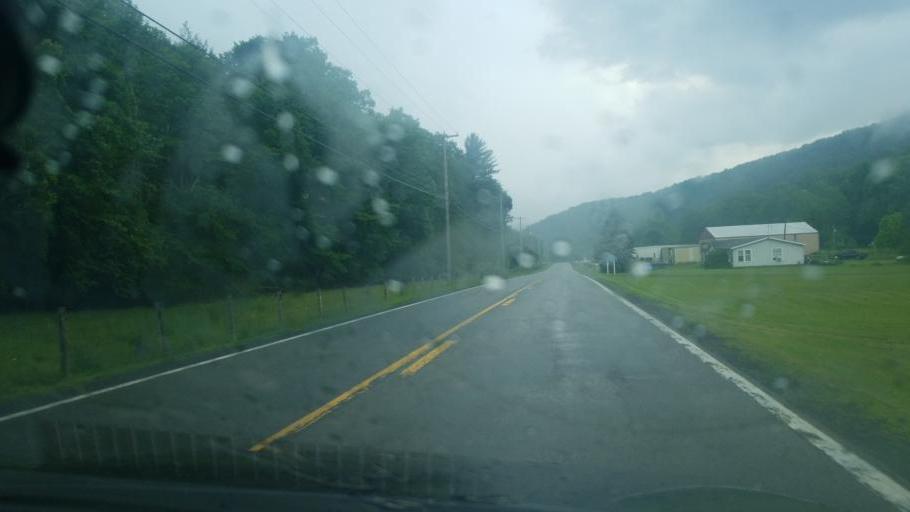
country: US
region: West Virginia
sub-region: Pendleton County
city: Franklin
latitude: 38.6723
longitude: -79.3018
